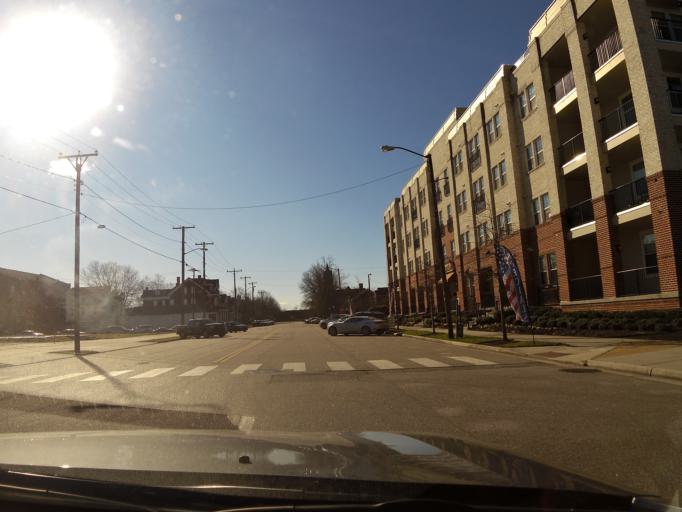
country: US
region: Virginia
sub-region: City of Portsmouth
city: Portsmouth
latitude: 36.8344
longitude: -76.3041
